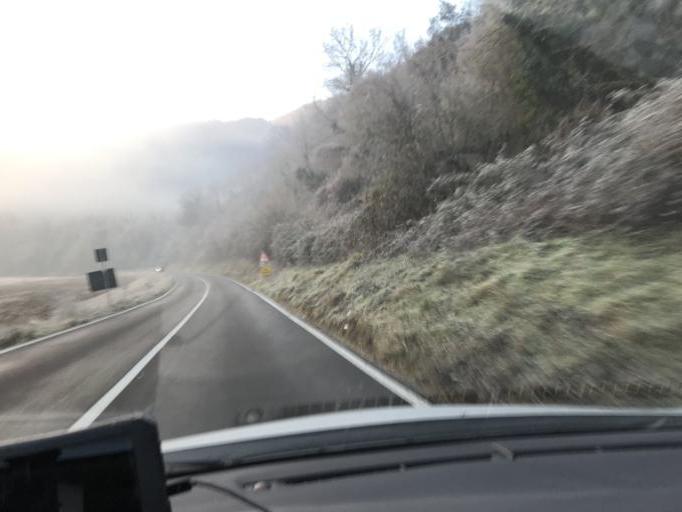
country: IT
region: Latium
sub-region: Provincia di Rieti
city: Colli sul Velino
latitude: 42.5218
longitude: 12.7343
